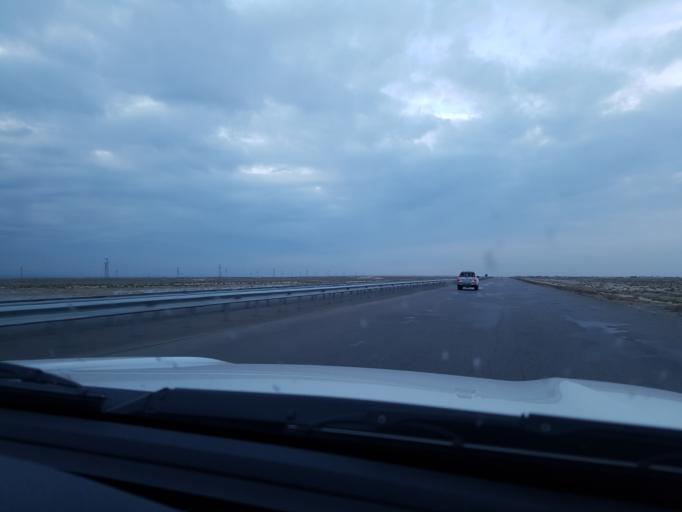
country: TM
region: Ahal
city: Kaka
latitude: 37.2840
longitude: 59.8001
